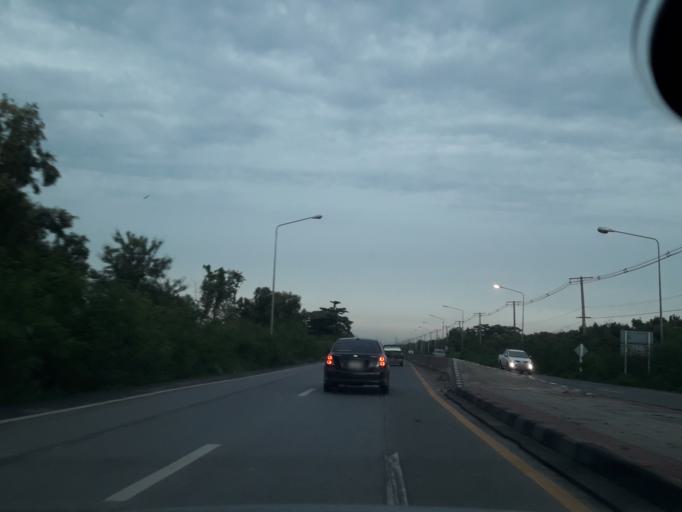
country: TH
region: Pathum Thani
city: Ban Rangsit
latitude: 14.0415
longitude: 100.7491
